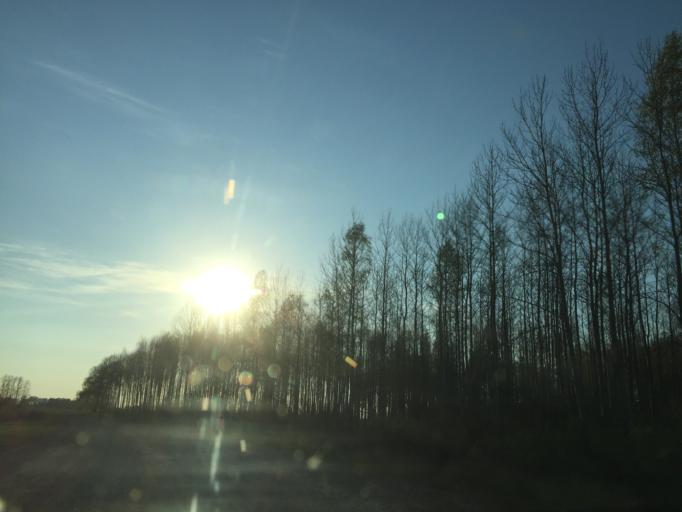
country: LV
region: Bauskas Rajons
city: Bauska
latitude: 56.2848
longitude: 24.2469
